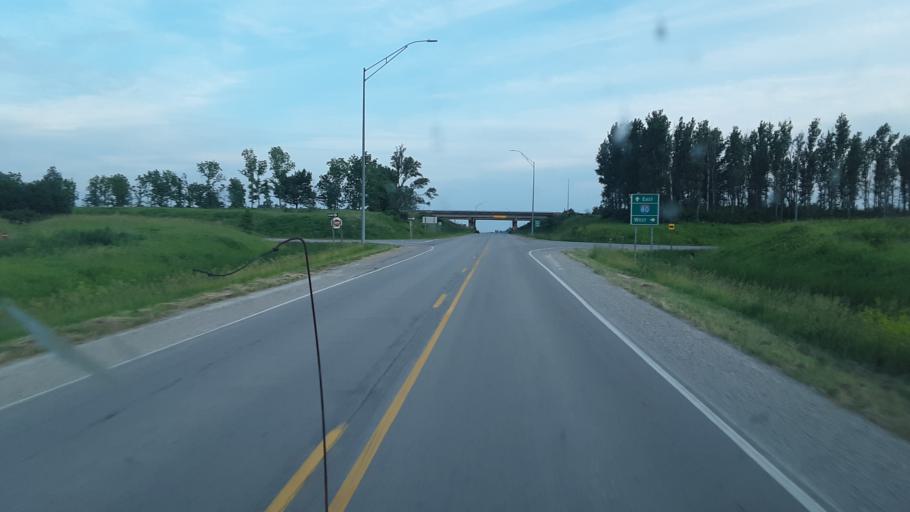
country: US
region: Iowa
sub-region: Iowa County
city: Marengo
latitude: 41.6981
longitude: -92.1625
